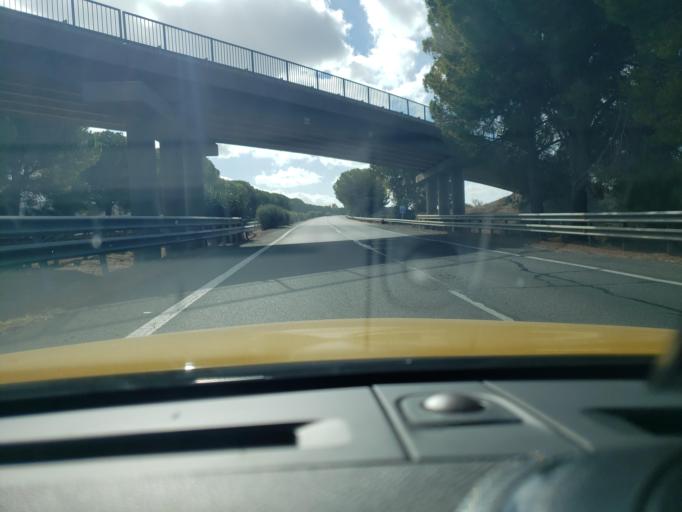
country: ES
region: Andalusia
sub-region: Provincia de Sevilla
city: Lebrija
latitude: 36.8641
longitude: -5.9943
